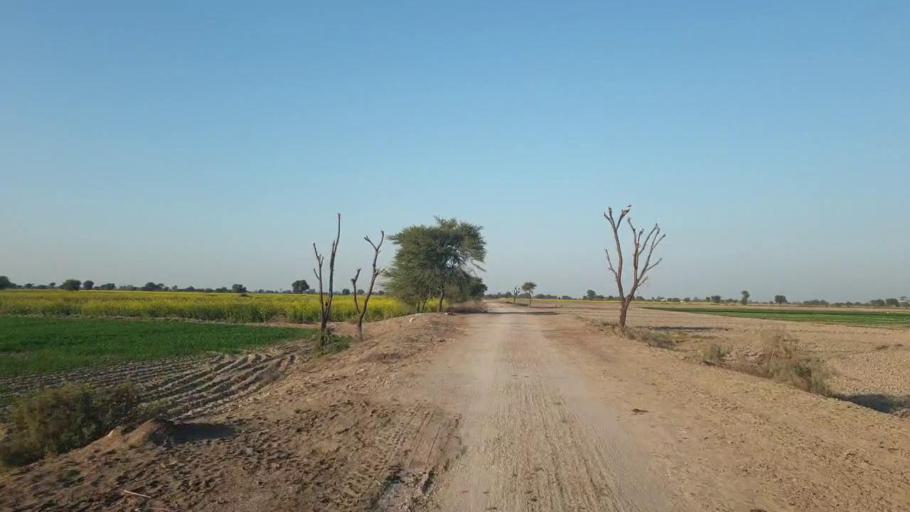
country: PK
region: Sindh
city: Shahpur Chakar
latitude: 26.0680
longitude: 68.6554
